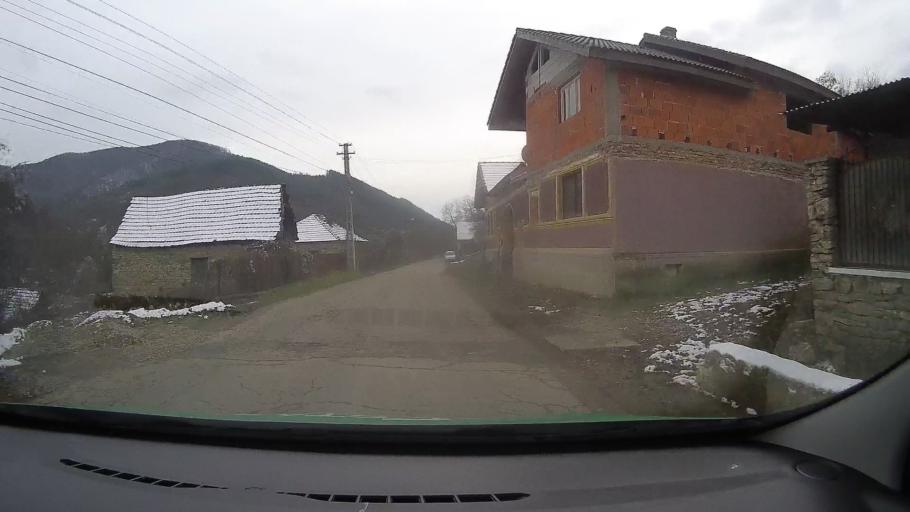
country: RO
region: Hunedoara
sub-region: Comuna Geoagiu
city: Geoagiu
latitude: 45.9752
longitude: 23.1702
